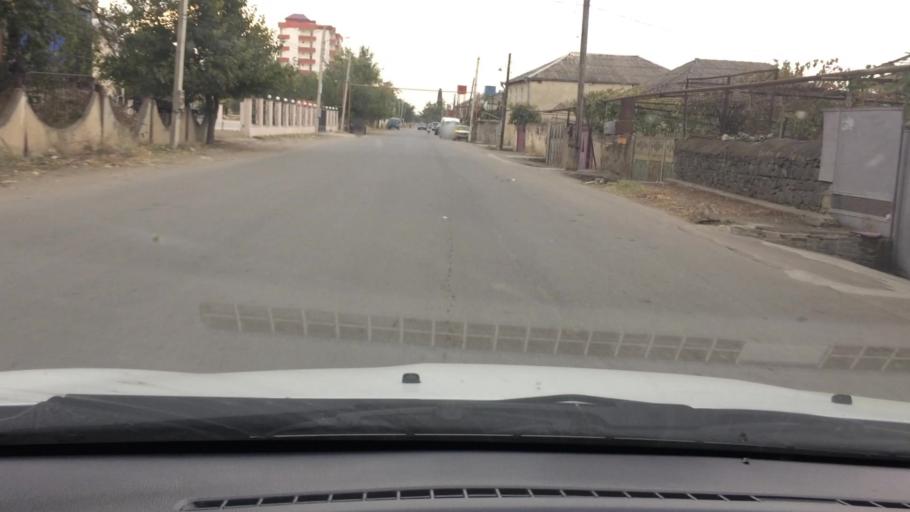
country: GE
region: Kvemo Kartli
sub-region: Marneuli
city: Marneuli
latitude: 41.4829
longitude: 44.7937
